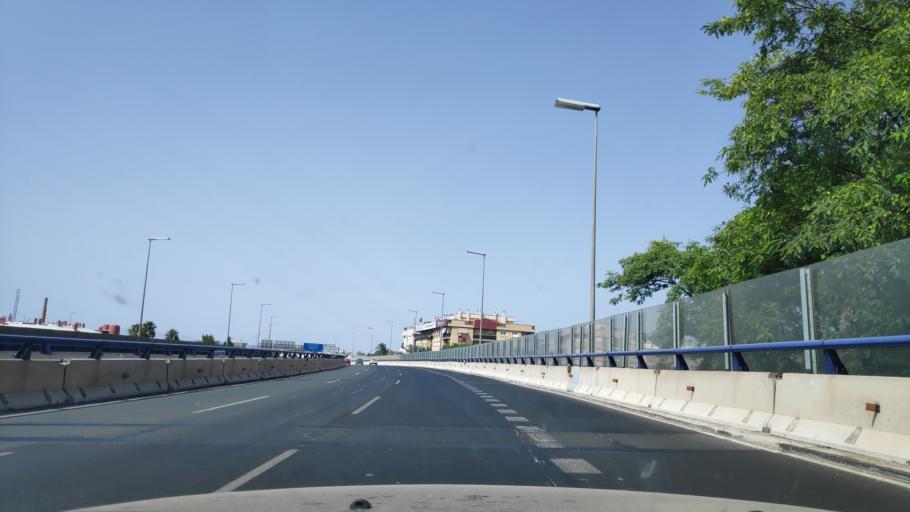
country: ES
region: Murcia
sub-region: Murcia
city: Murcia
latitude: 37.9739
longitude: -1.1366
